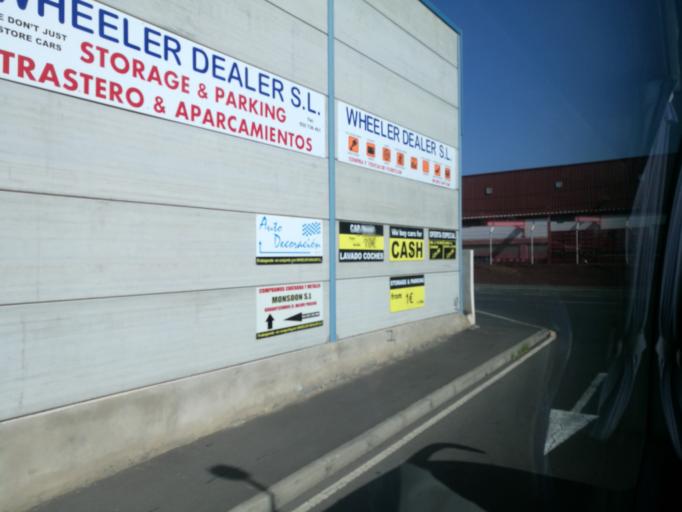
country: ES
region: Canary Islands
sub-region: Provincia de Santa Cruz de Tenerife
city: Las Rosas
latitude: 28.0478
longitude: -16.6190
